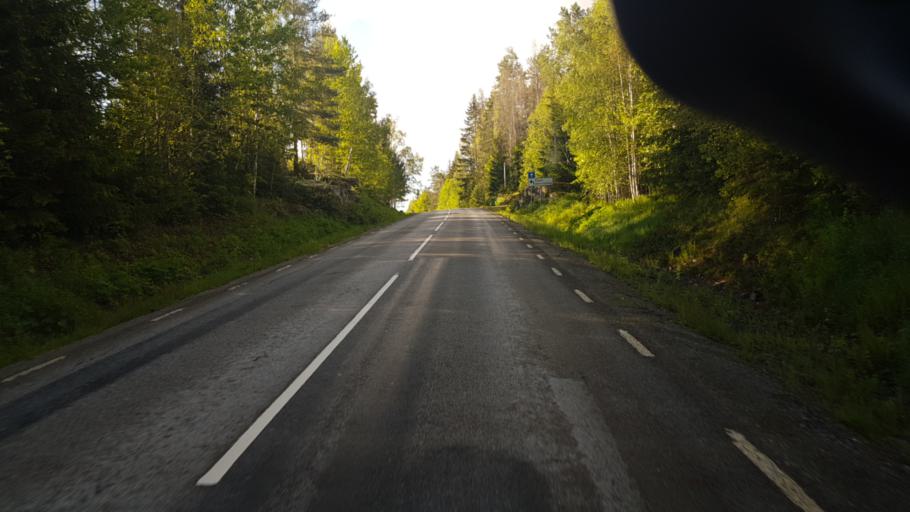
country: SE
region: Vaermland
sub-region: Arvika Kommun
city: Arvika
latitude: 59.6187
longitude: 12.5097
